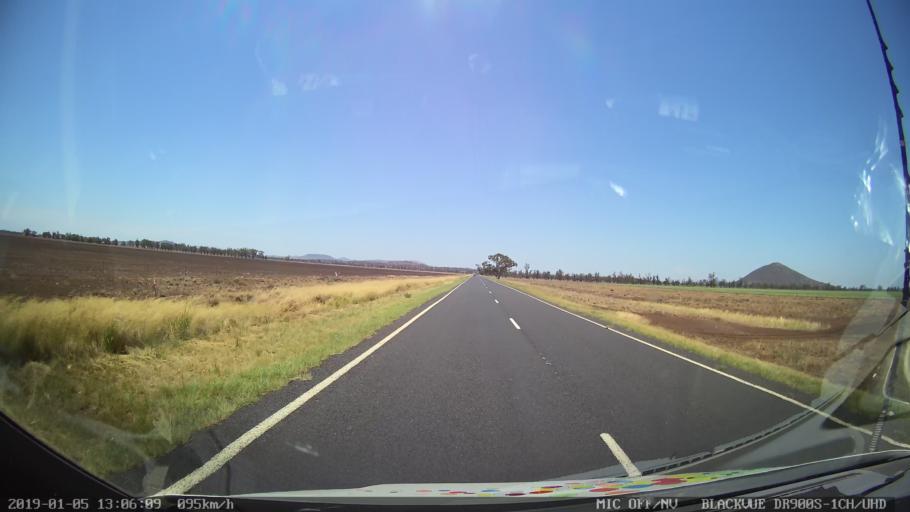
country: AU
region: New South Wales
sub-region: Gunnedah
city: Gunnedah
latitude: -31.0950
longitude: 149.8645
